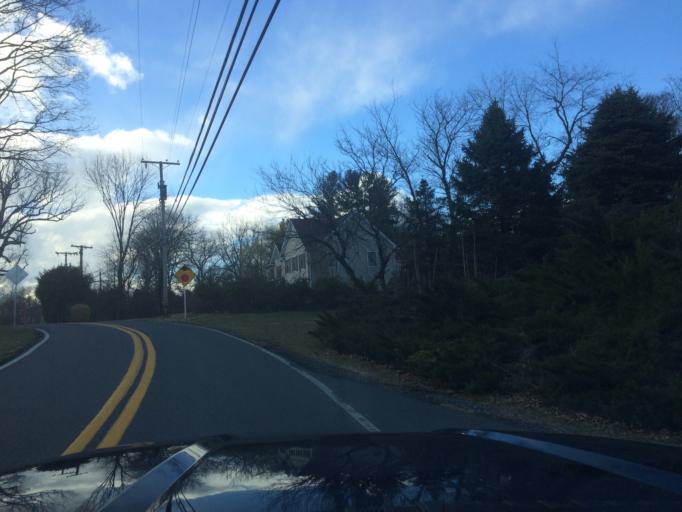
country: US
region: Maryland
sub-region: Carroll County
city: Eldersburg
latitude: 39.3777
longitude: -76.9080
